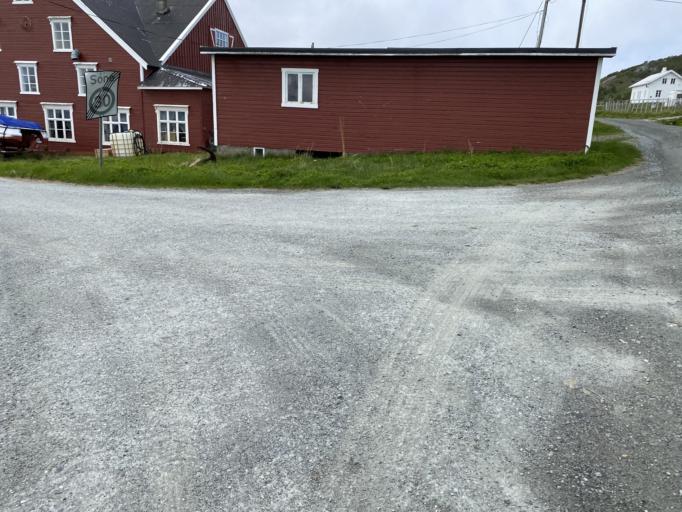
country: NO
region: Troms
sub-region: Karlsoy
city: Hansnes
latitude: 70.0025
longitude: 19.8900
